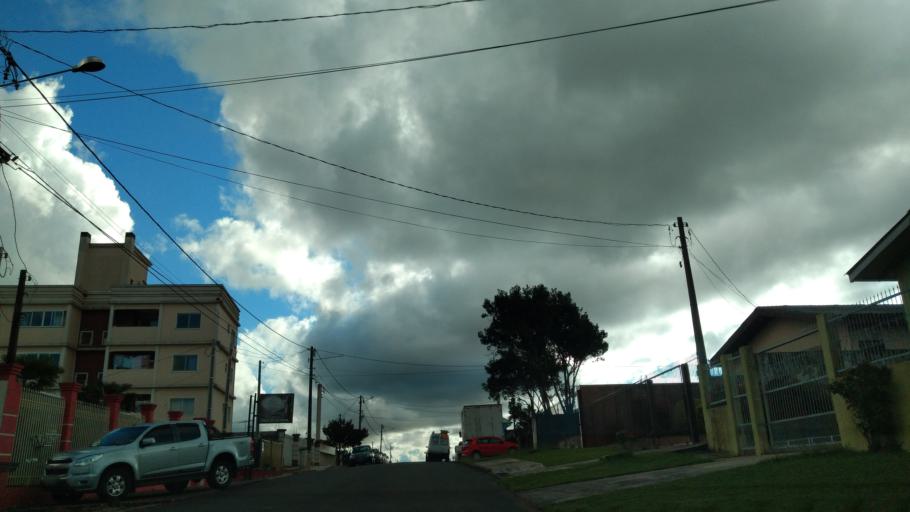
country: BR
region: Parana
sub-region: Guarapuava
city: Guarapuava
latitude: -25.3976
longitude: -51.4890
